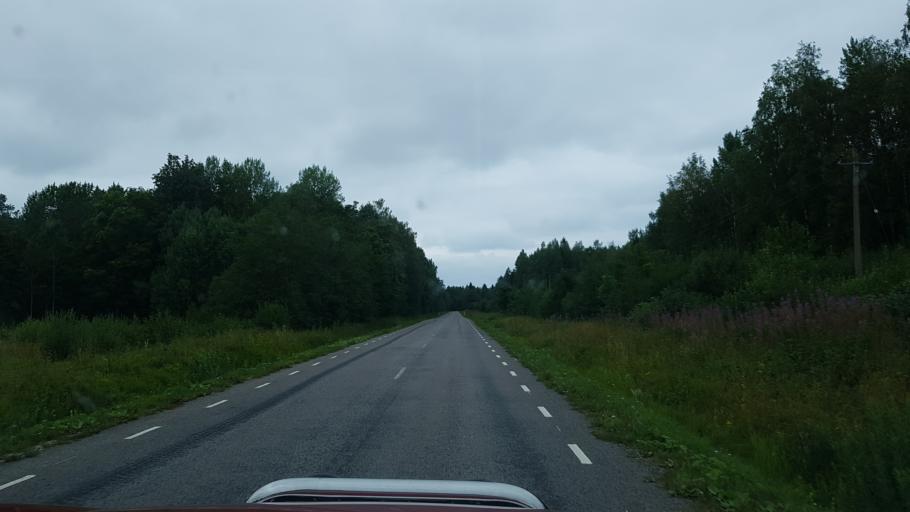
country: EE
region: Ida-Virumaa
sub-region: Johvi vald
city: Johvi
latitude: 59.4249
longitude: 27.4034
